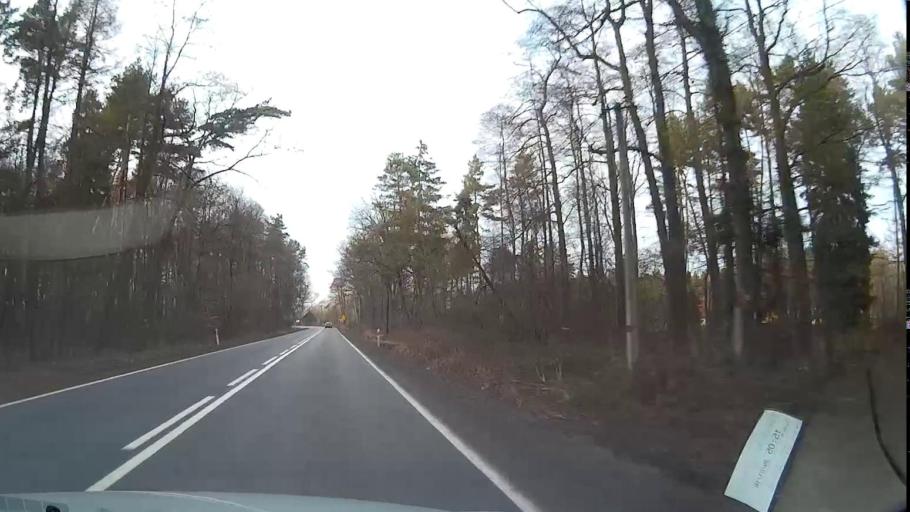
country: PL
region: Lesser Poland Voivodeship
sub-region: Powiat chrzanowski
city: Brodla
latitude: 50.0385
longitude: 19.6016
